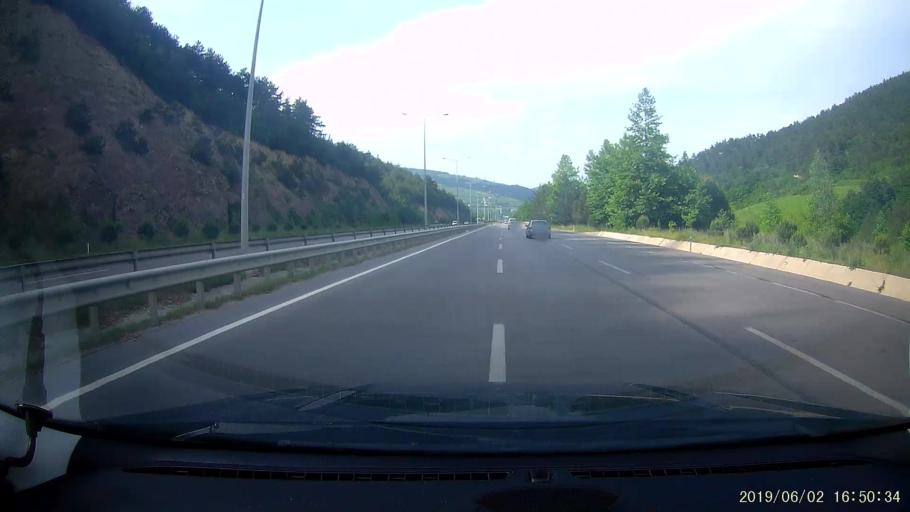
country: TR
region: Samsun
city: Taflan
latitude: 41.2575
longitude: 36.1740
